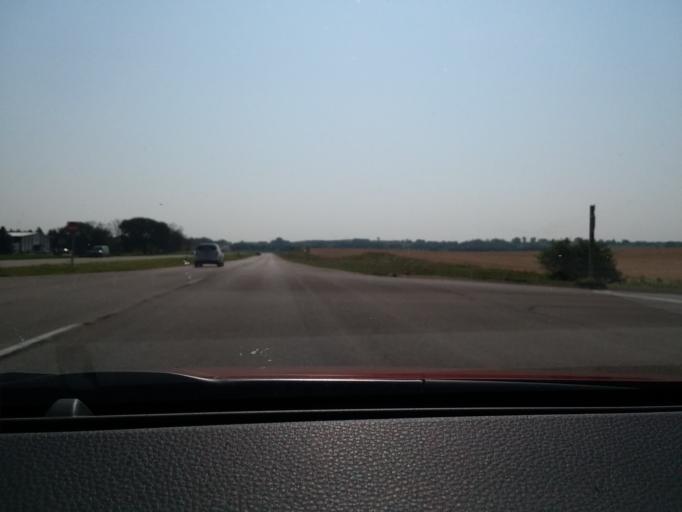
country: US
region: Wisconsin
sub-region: Dane County
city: Waunakee
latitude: 43.1915
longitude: -89.4219
